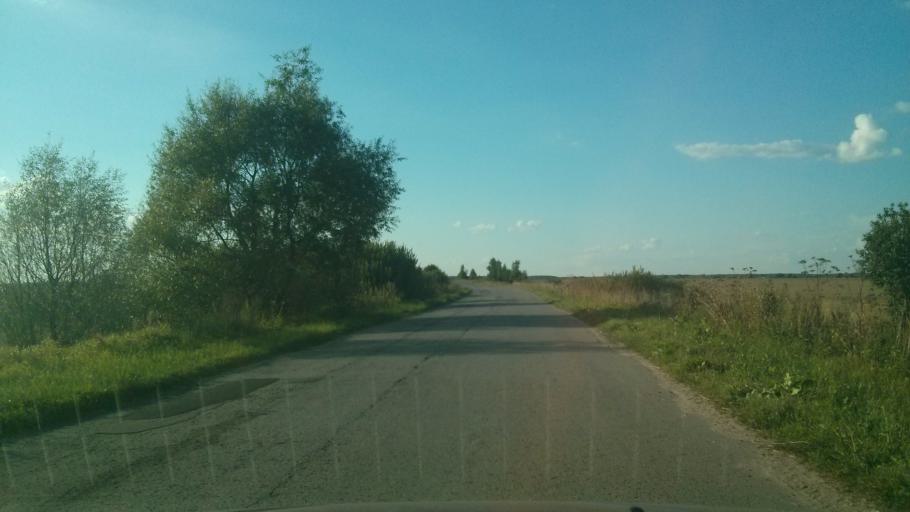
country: RU
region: Vladimir
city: Melenki
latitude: 55.2964
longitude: 41.7949
